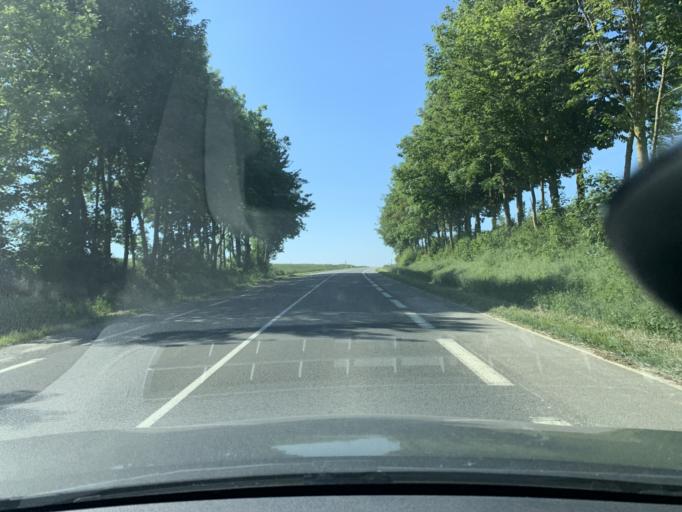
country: FR
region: Nord-Pas-de-Calais
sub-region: Departement du Nord
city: Rumilly-en-Cambresis
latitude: 50.1253
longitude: 3.2462
